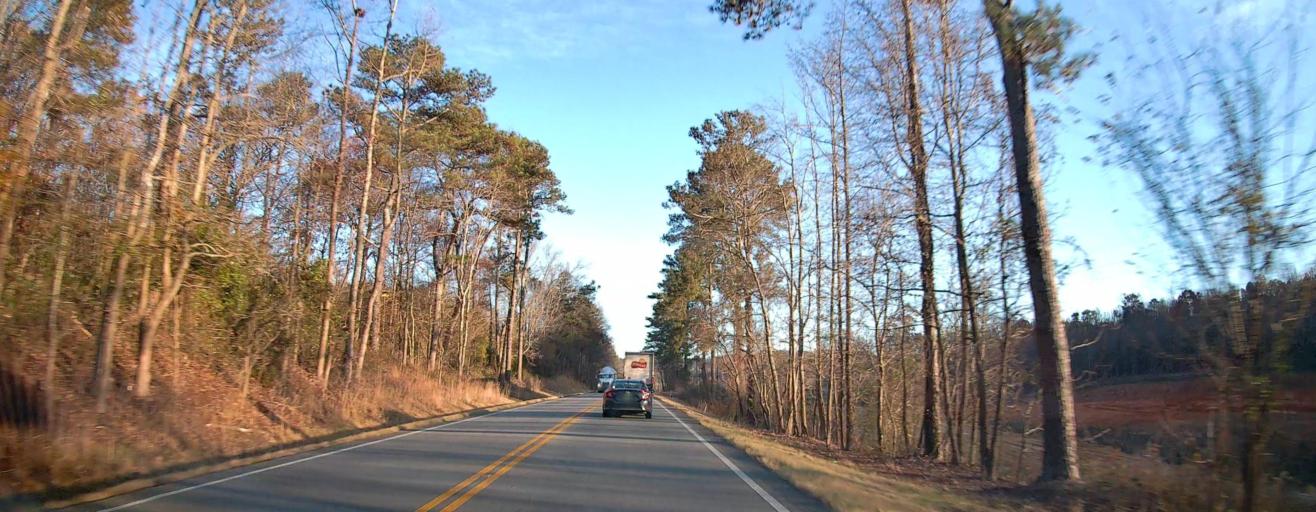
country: US
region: Alabama
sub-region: Blount County
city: Oneonta
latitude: 34.0763
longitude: -86.3343
